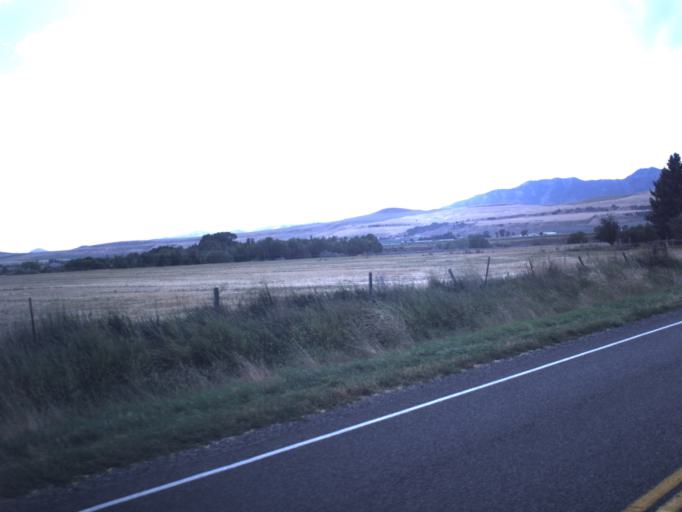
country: US
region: Utah
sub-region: Cache County
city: Lewiston
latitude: 41.9754
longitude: -111.9275
